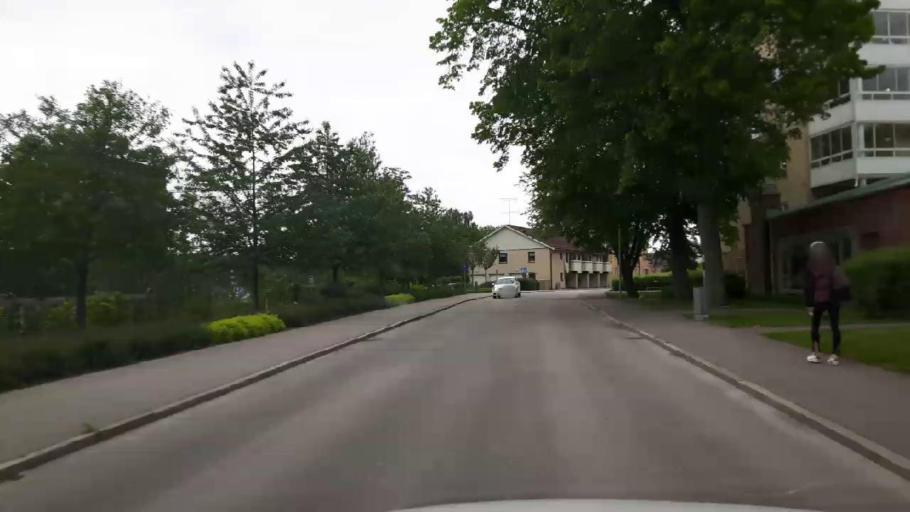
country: SE
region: Vaestmanland
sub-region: Kopings Kommun
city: Koping
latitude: 59.5163
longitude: 15.9889
